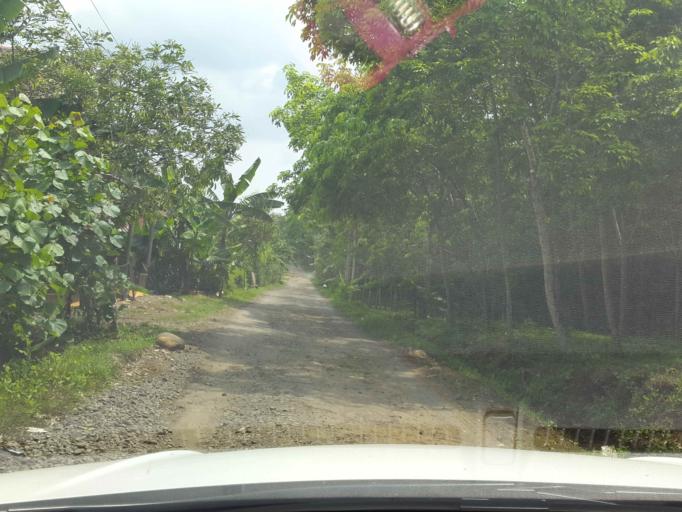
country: ID
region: Central Java
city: Cilongkrang
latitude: -7.4133
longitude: 108.7227
